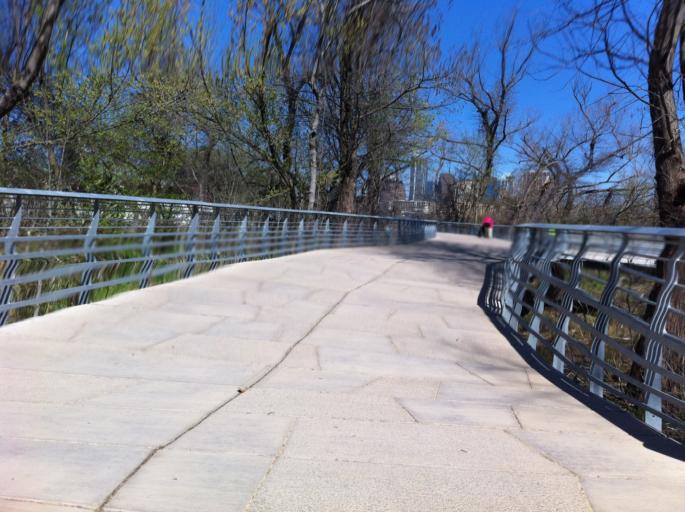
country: US
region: Texas
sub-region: Travis County
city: Austin
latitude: 30.2519
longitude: -97.7403
